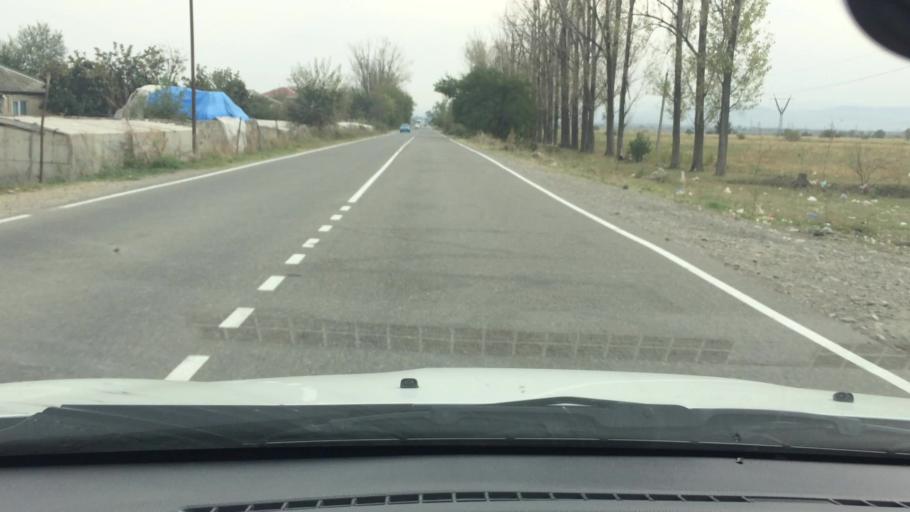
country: GE
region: Kvemo Kartli
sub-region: Gardabani
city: Gardabani
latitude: 41.4472
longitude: 44.9959
